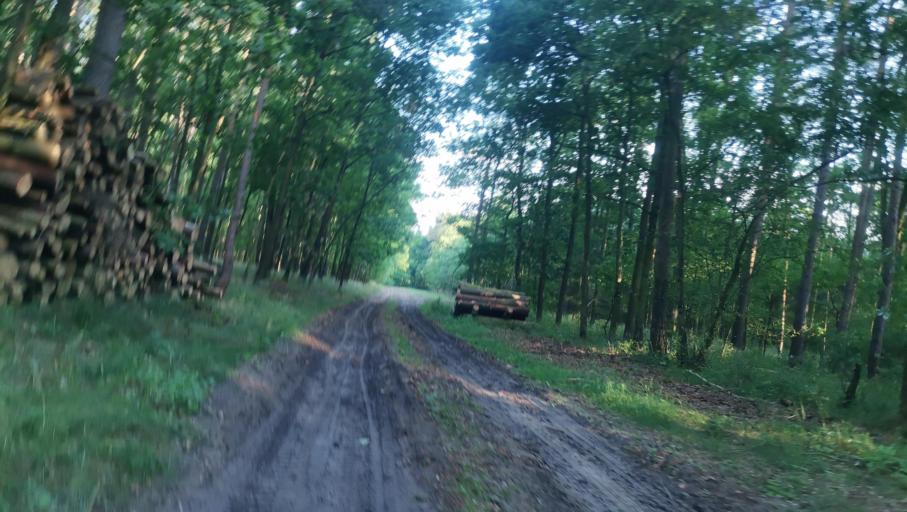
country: PL
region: Greater Poland Voivodeship
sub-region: Powiat jarocinski
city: Jarocin
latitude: 51.9834
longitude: 17.5438
